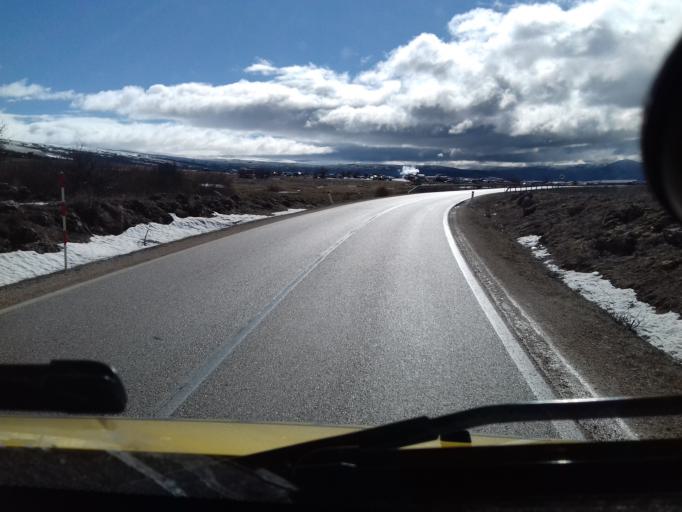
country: BA
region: Federation of Bosnia and Herzegovina
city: Tomislavgrad
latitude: 43.7739
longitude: 17.2325
